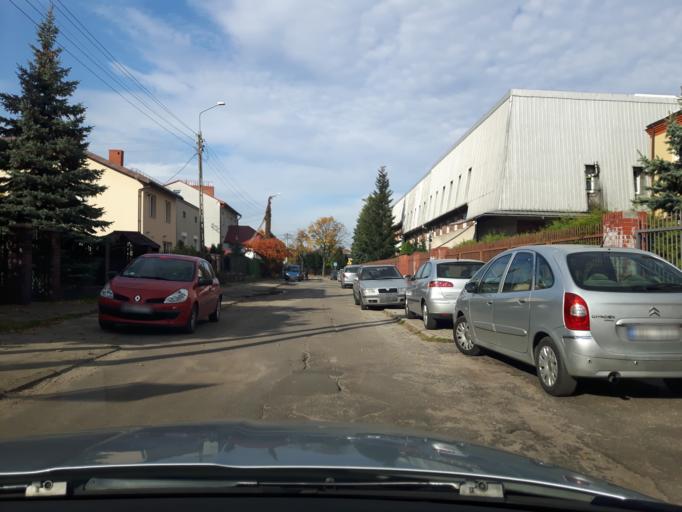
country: PL
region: Masovian Voivodeship
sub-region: Powiat wolominski
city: Zabki
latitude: 52.2988
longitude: 21.0973
